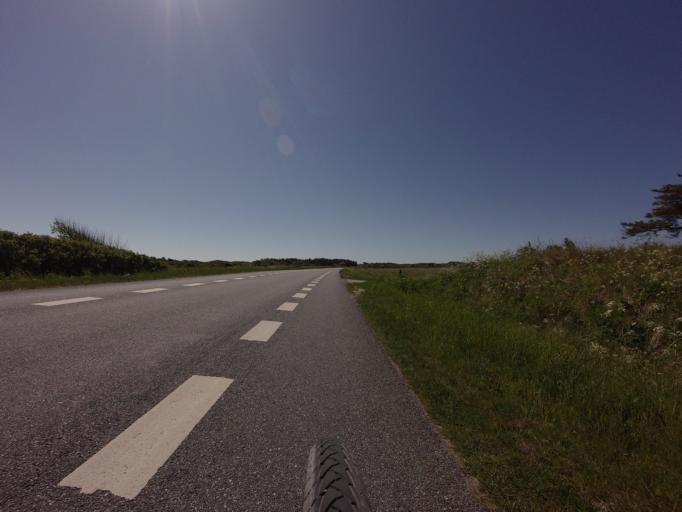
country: DK
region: North Denmark
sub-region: Hjorring Kommune
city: Hjorring
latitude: 57.4541
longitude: 9.7968
